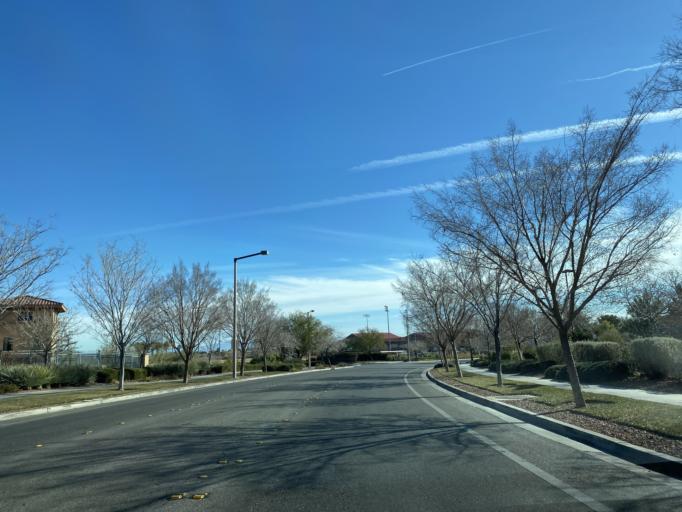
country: US
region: Nevada
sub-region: Clark County
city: Summerlin South
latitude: 36.1568
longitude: -115.3208
